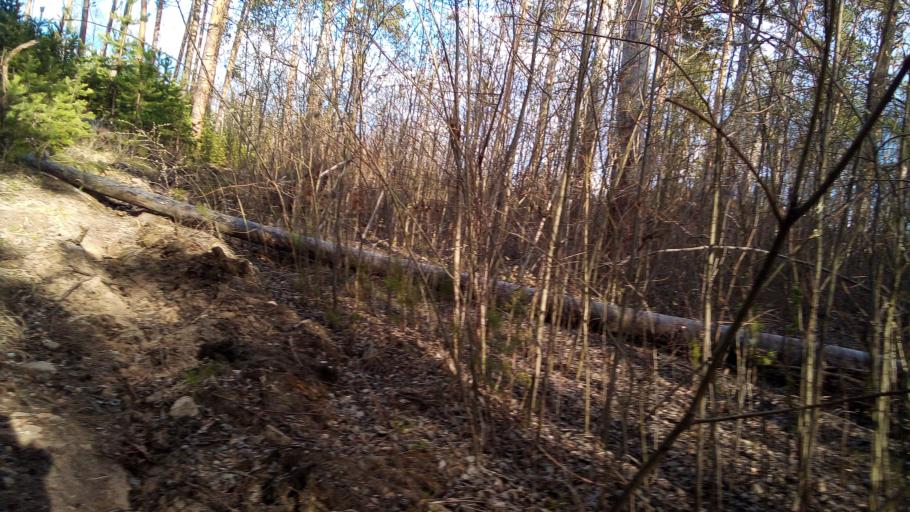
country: RU
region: Chelyabinsk
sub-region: Gorod Chelyabinsk
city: Chelyabinsk
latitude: 55.1640
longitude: 61.3221
